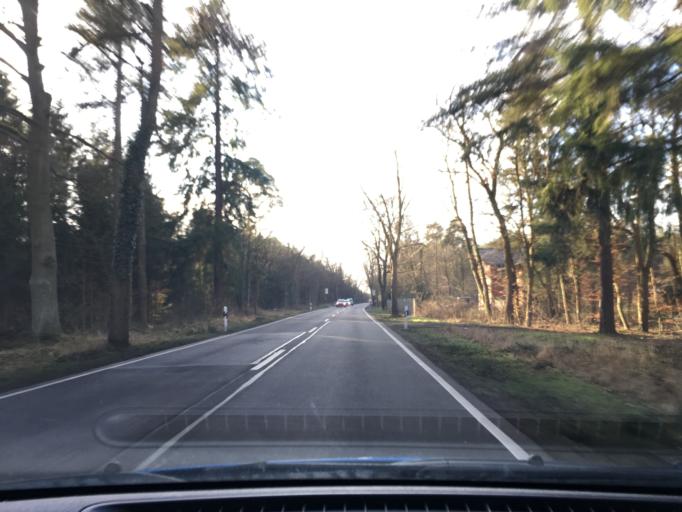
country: DE
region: Saxony-Anhalt
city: Seehausen
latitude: 52.8843
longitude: 11.6458
